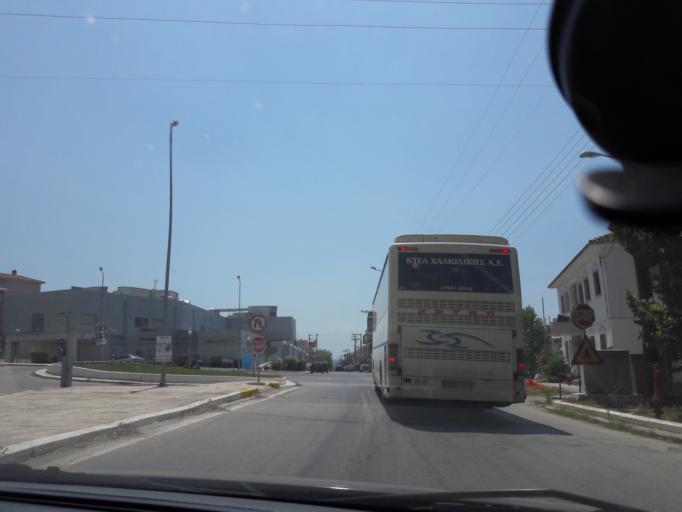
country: GR
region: Central Macedonia
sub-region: Nomos Chalkidikis
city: Nea Kallikrateia
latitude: 40.3176
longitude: 23.0639
